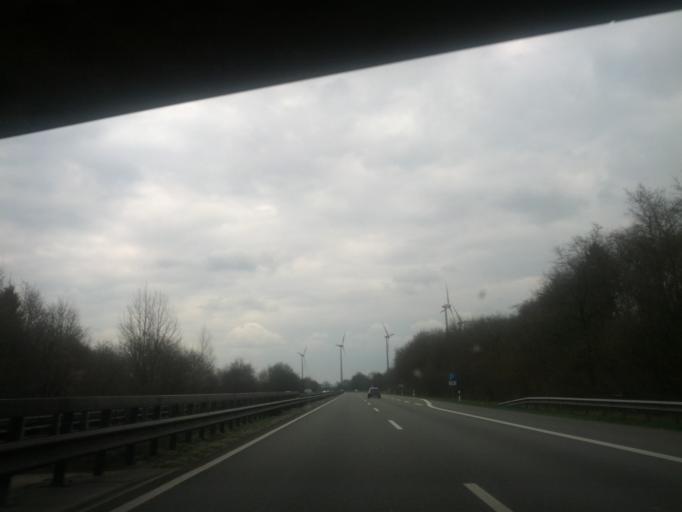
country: DE
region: Lower Saxony
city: Hatten
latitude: 53.0595
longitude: 8.3841
